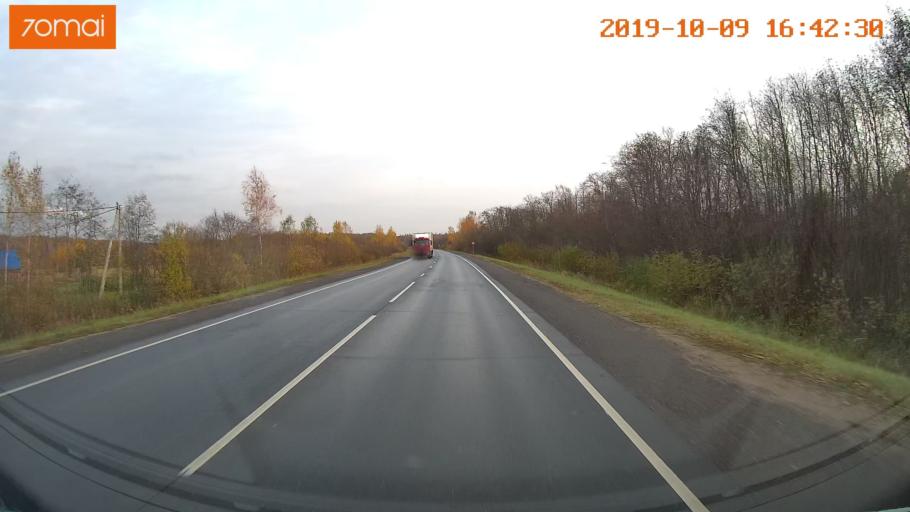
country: RU
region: Kostroma
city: Volgorechensk
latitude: 57.4613
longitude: 41.1015
